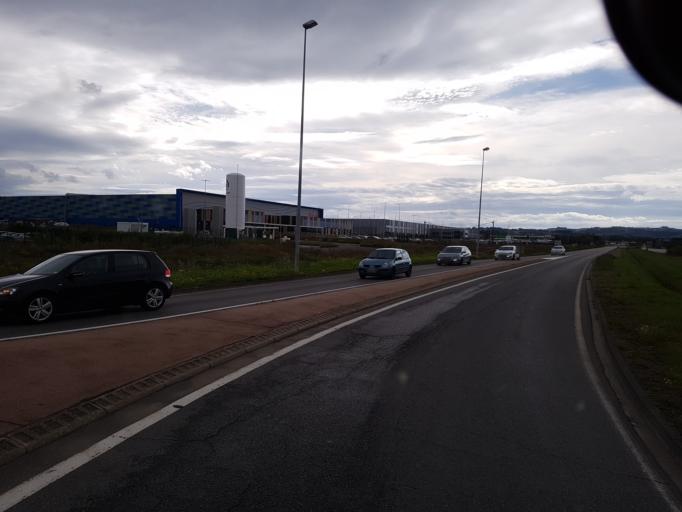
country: FR
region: Rhone-Alpes
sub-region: Departement de la Loire
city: Veauche
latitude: 45.5456
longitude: 4.3056
